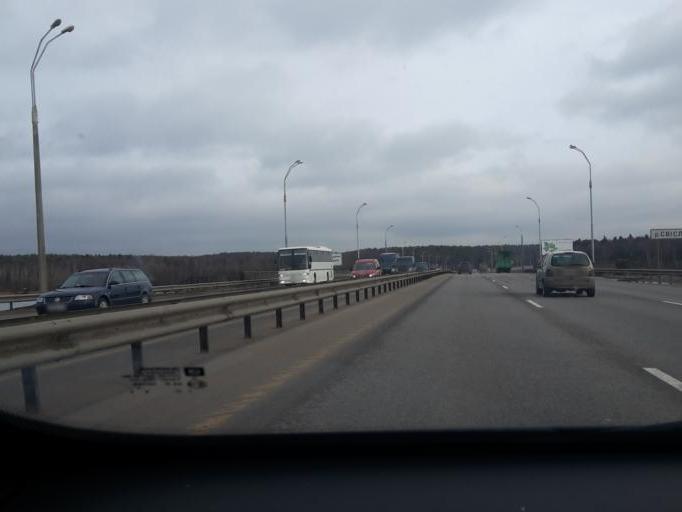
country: BY
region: Minsk
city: Zhdanovichy
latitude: 53.9572
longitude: 27.4539
